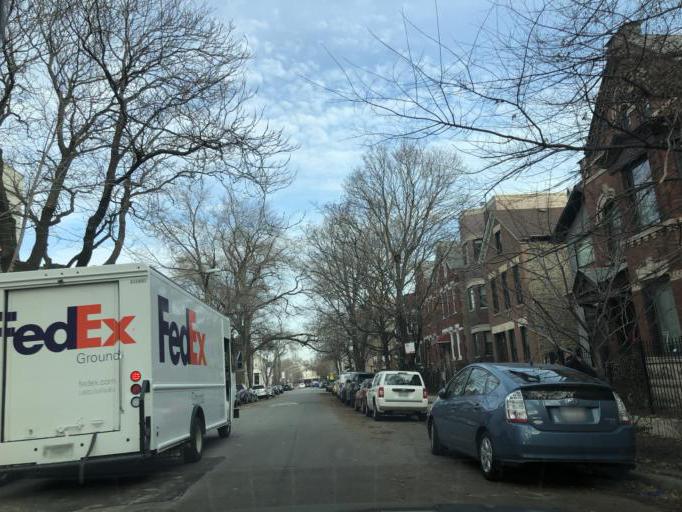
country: US
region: Illinois
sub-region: Cook County
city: Chicago
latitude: 41.9003
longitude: -87.6735
